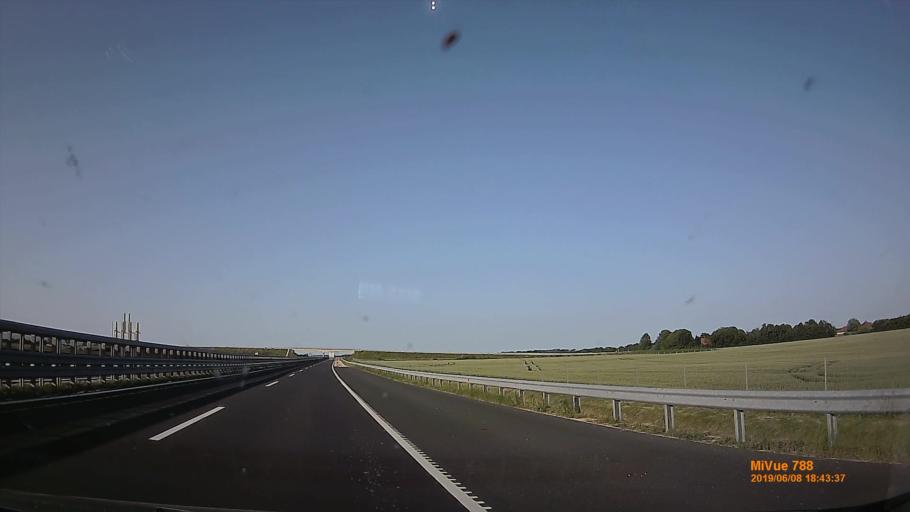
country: HU
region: Gyor-Moson-Sopron
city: Beled
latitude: 47.4571
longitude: 17.1105
